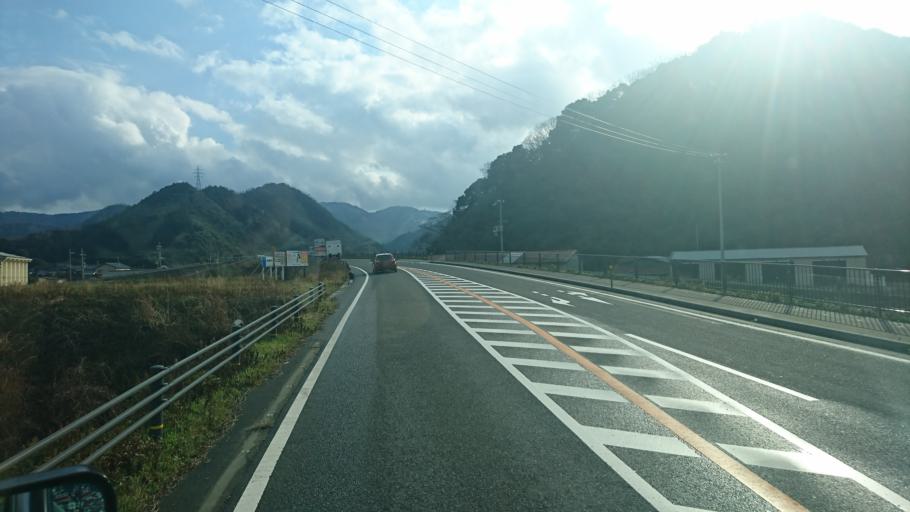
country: JP
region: Tottori
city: Tottori
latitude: 35.6097
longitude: 134.4703
